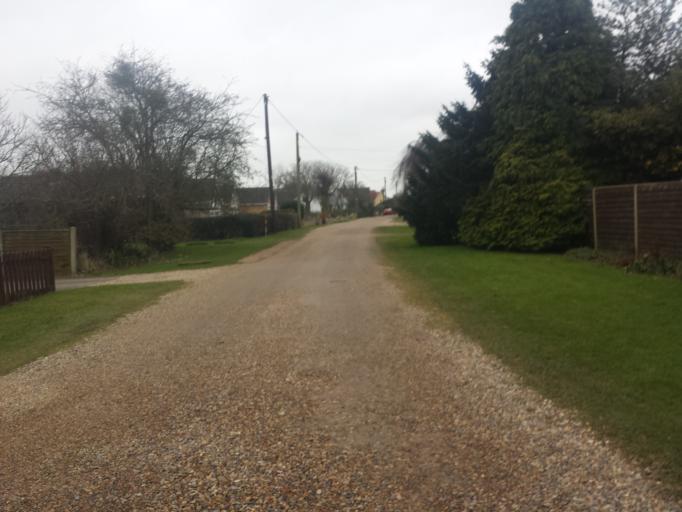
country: GB
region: England
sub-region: Essex
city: Little Clacton
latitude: 51.8612
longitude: 1.1601
